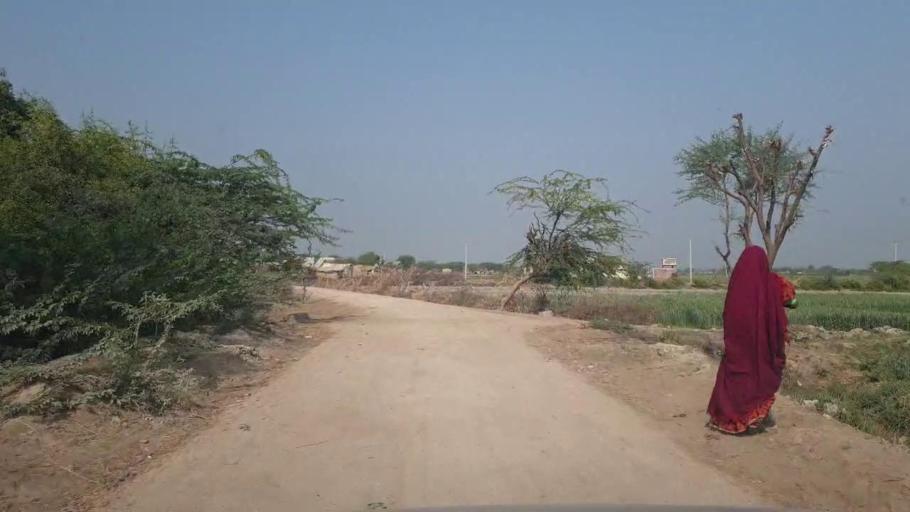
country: PK
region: Sindh
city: Umarkot
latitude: 25.3996
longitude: 69.6986
